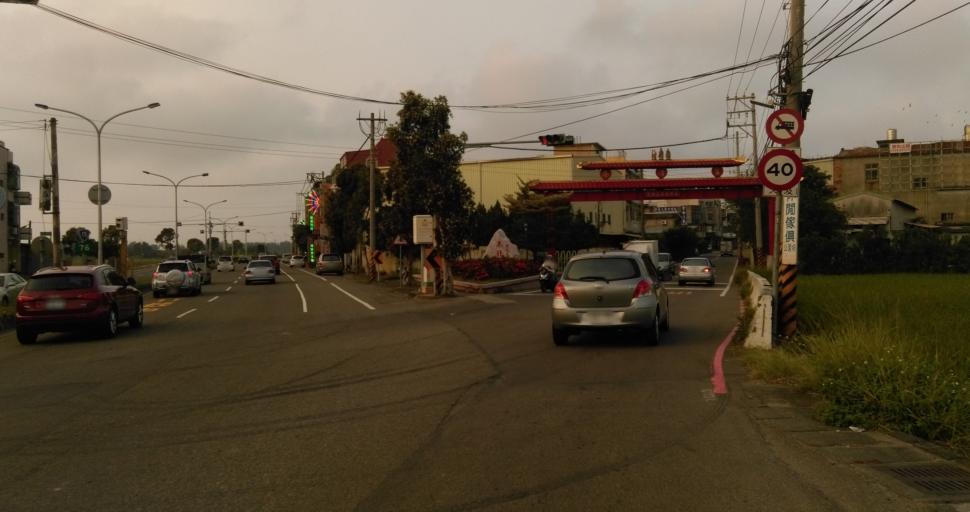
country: TW
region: Taiwan
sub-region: Hsinchu
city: Hsinchu
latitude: 24.8272
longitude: 120.9277
